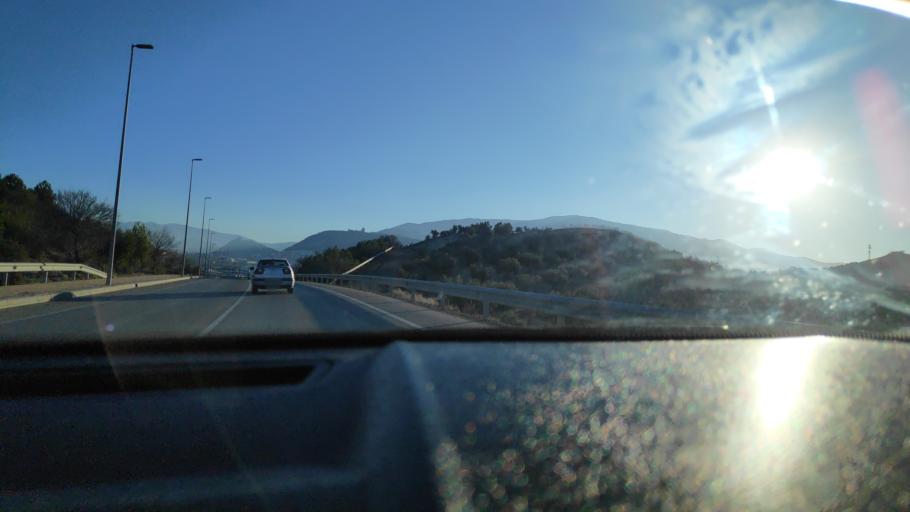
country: ES
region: Andalusia
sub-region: Provincia de Jaen
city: Jaen
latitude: 37.8070
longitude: -3.7880
